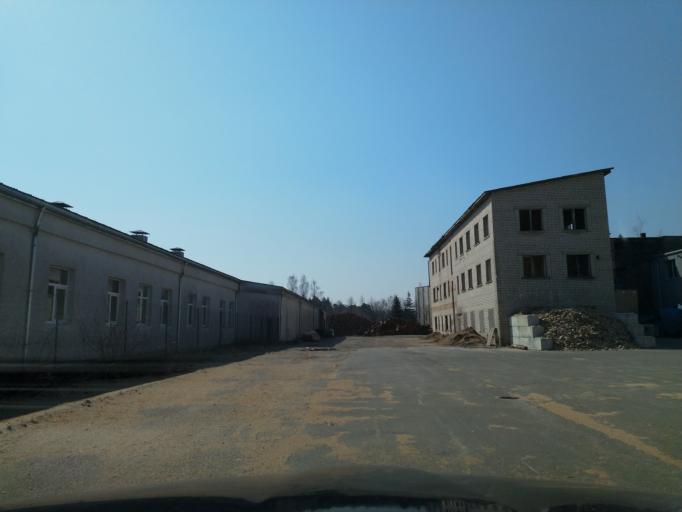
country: LV
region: Kuldigas Rajons
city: Kuldiga
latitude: 56.9670
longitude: 21.9248
